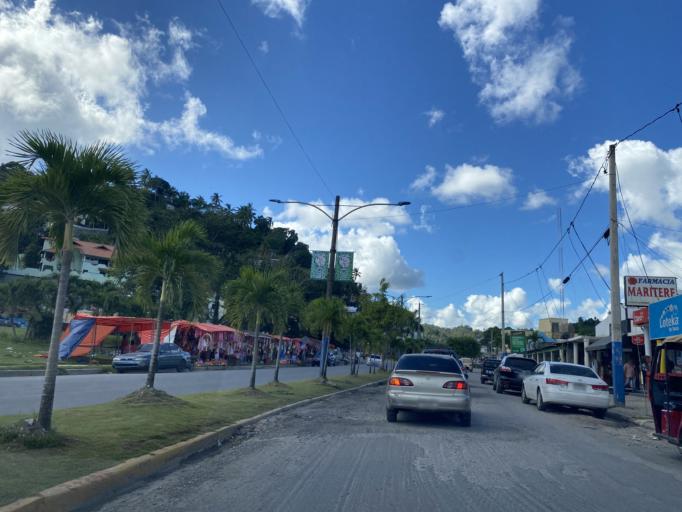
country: DO
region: Samana
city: Samana
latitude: 19.2032
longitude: -69.3391
